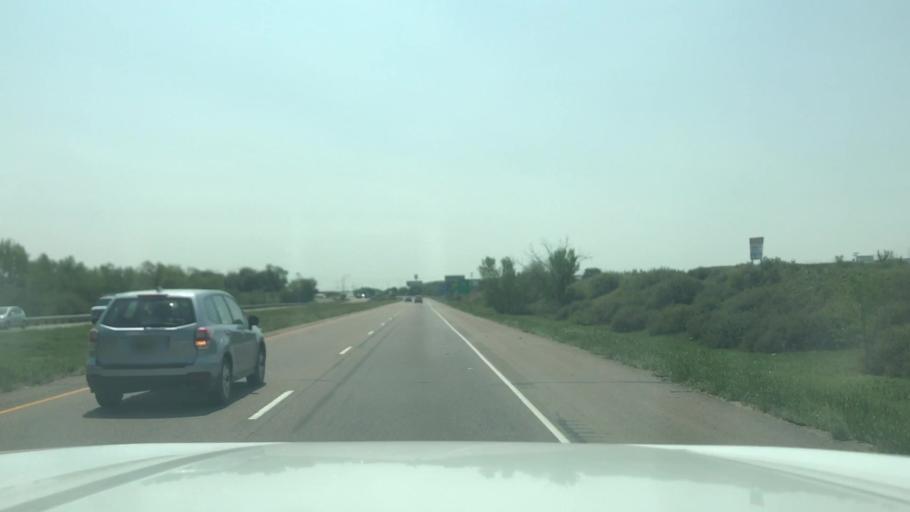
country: US
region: Colorado
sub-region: El Paso County
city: Fountain
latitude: 38.6827
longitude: -104.7154
